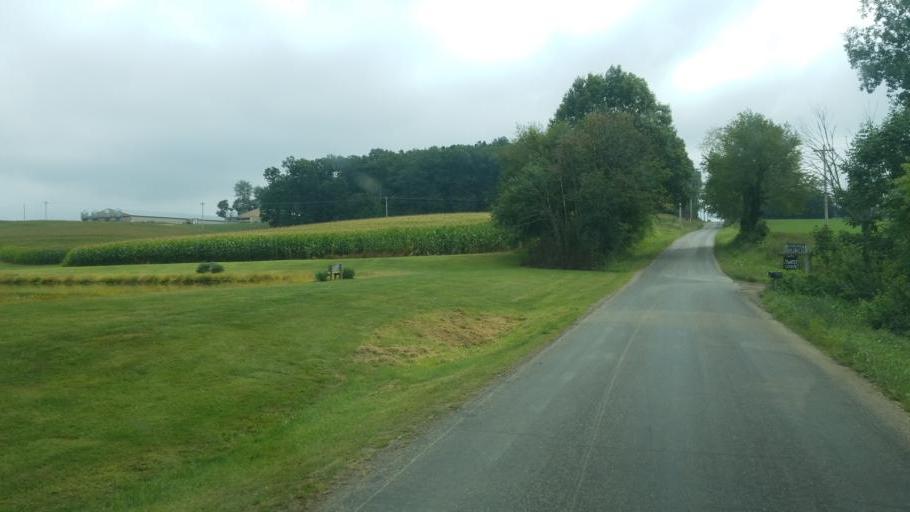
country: US
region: Ohio
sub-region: Licking County
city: Utica
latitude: 40.2561
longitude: -82.3745
